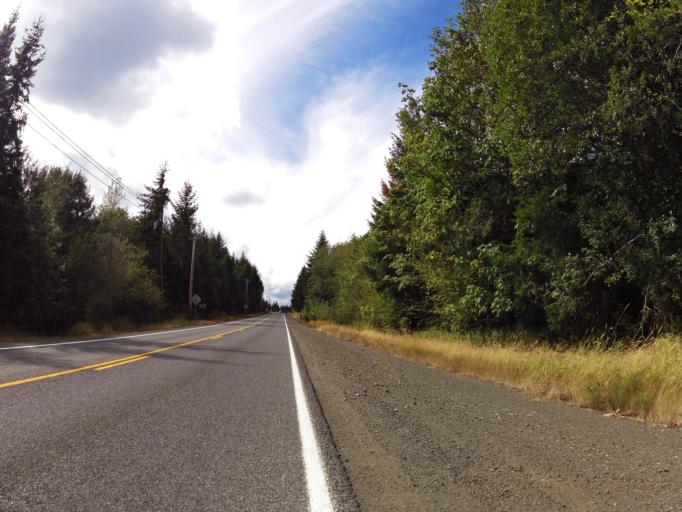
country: US
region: Washington
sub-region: Mason County
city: Shelton
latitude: 47.1494
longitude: -123.0658
